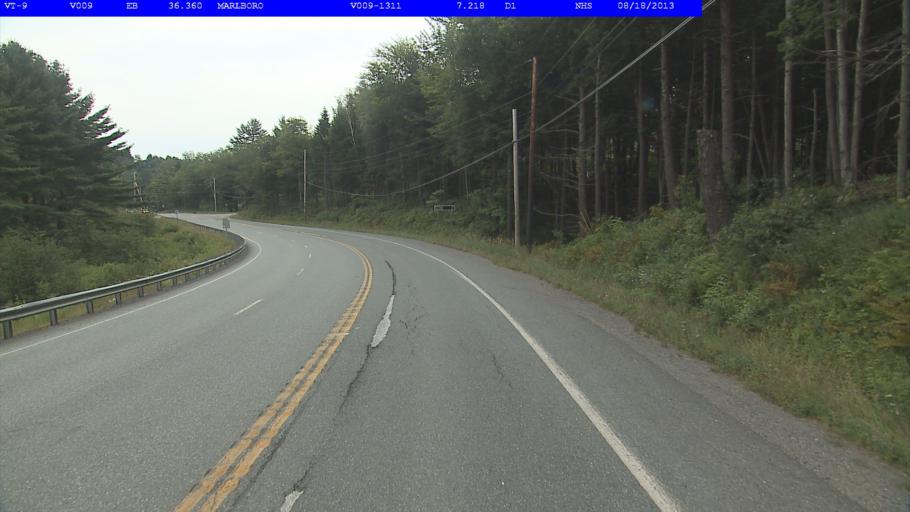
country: US
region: Vermont
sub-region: Windham County
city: West Brattleboro
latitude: 42.8786
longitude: -72.6964
